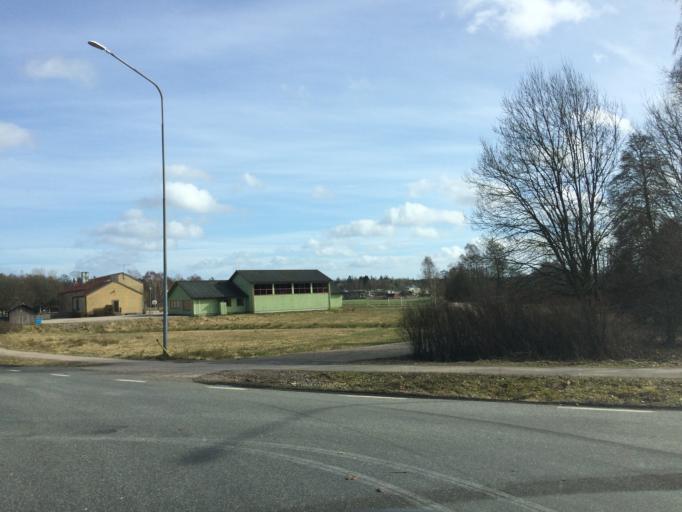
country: SE
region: Halland
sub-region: Hylte Kommun
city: Torup
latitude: 57.0264
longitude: 13.0991
